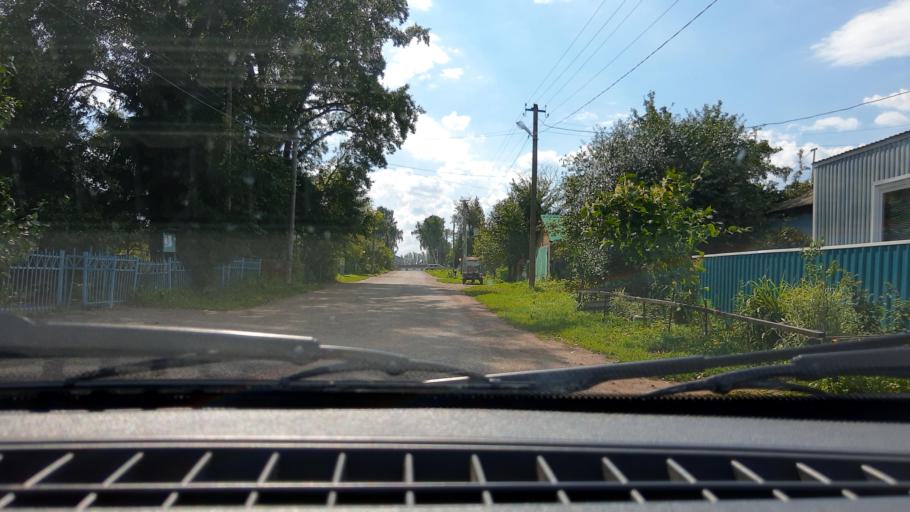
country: RU
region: Bashkortostan
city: Mikhaylovka
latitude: 54.8648
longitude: 55.8163
